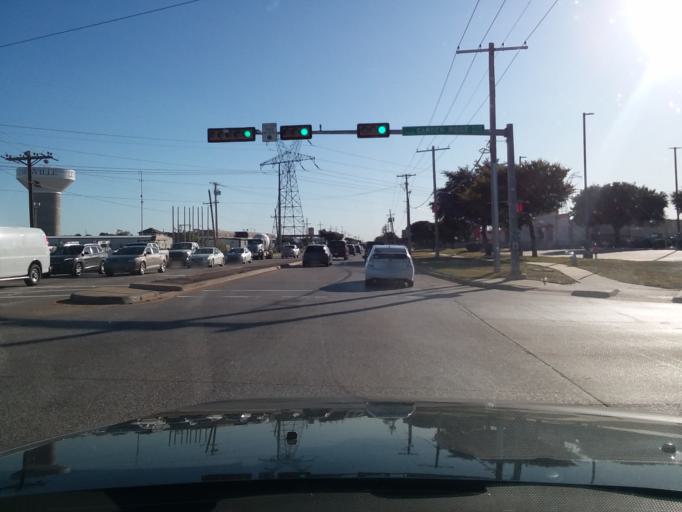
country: US
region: Texas
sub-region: Denton County
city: Highland Village
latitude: 33.0714
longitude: -97.0356
